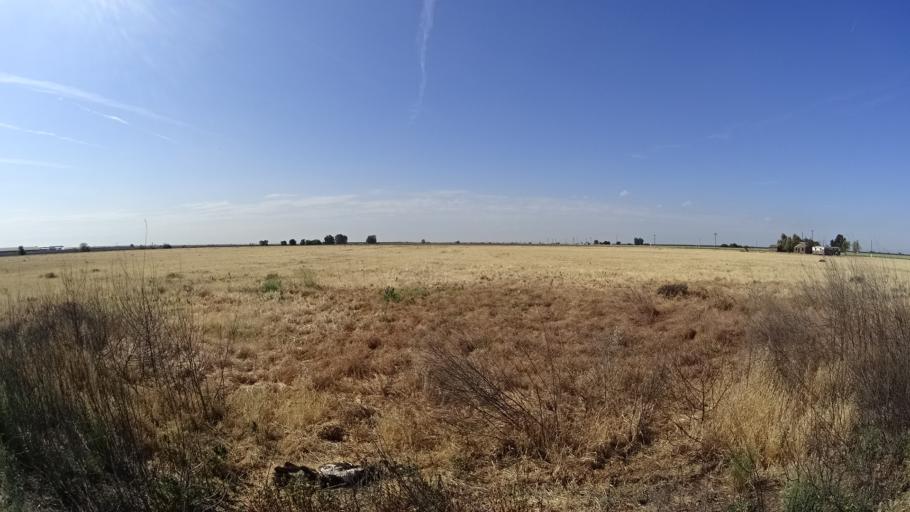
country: US
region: California
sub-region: Kings County
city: Home Garden
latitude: 36.2261
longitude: -119.5634
